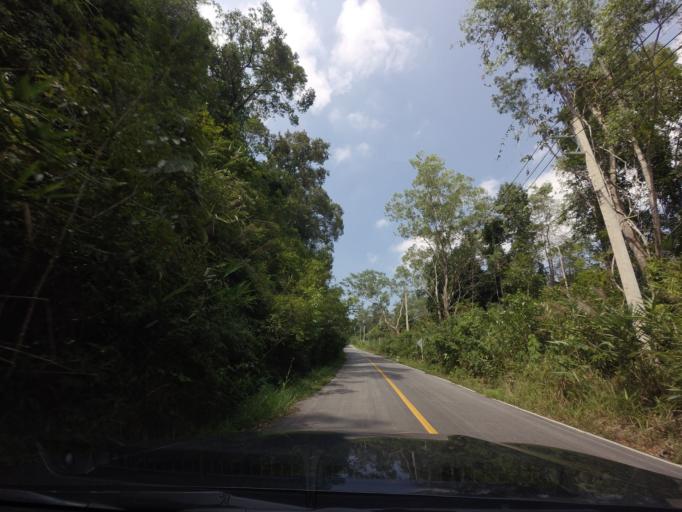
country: TH
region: Loei
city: Na Haeo
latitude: 17.4723
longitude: 100.9356
